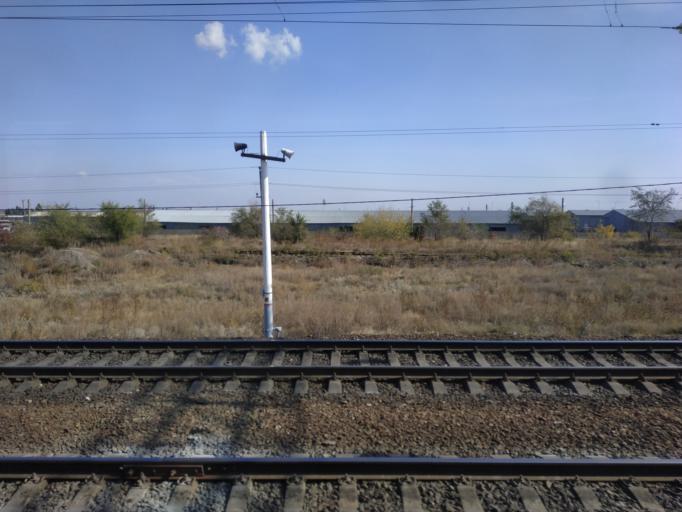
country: RU
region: Volgograd
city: Gumrak
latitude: 48.7897
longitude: 44.3684
